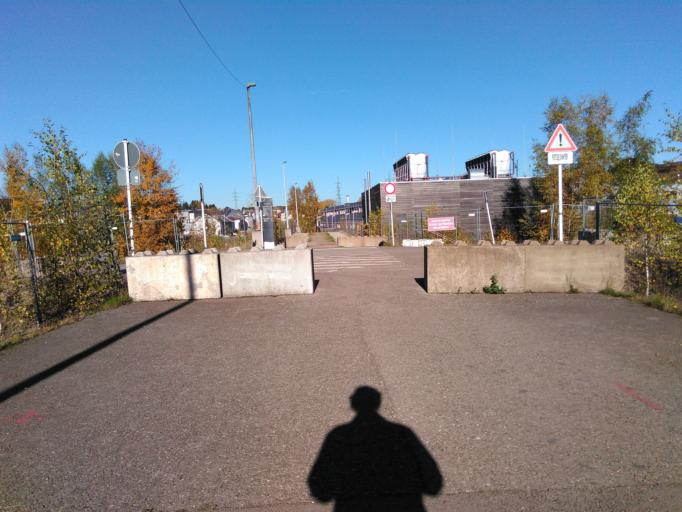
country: LU
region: Luxembourg
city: Belvaux
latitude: 49.5050
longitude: 5.9425
